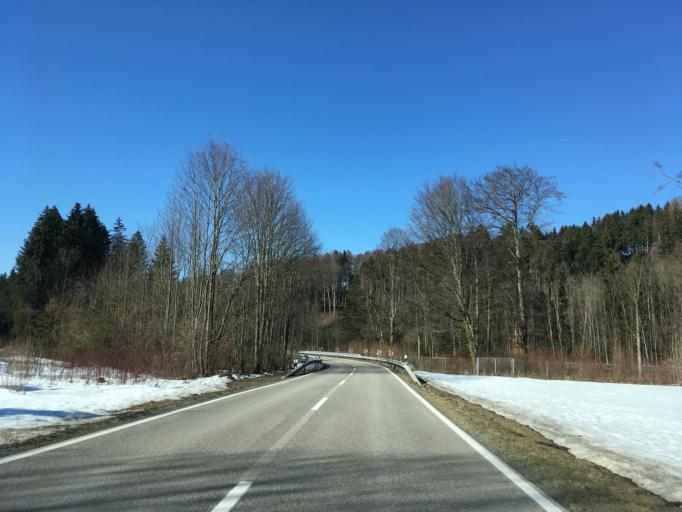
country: DE
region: Bavaria
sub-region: Upper Bavaria
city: Frasdorf
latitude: 47.7975
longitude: 12.2551
